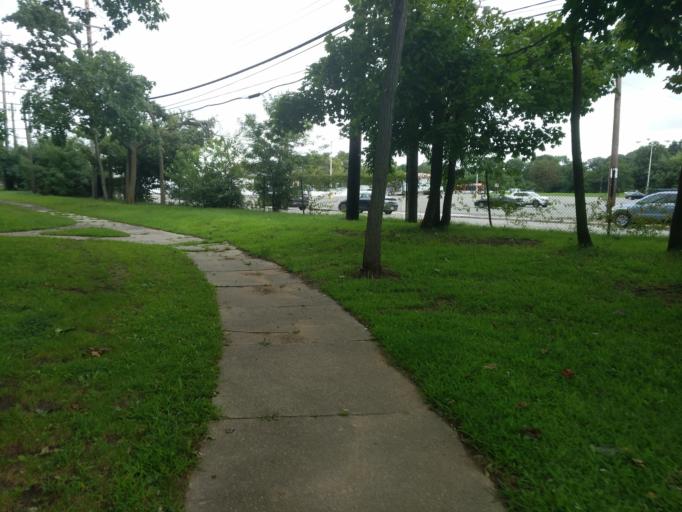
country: US
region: New York
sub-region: Nassau County
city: Valley Stream
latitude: 40.6616
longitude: -73.7116
